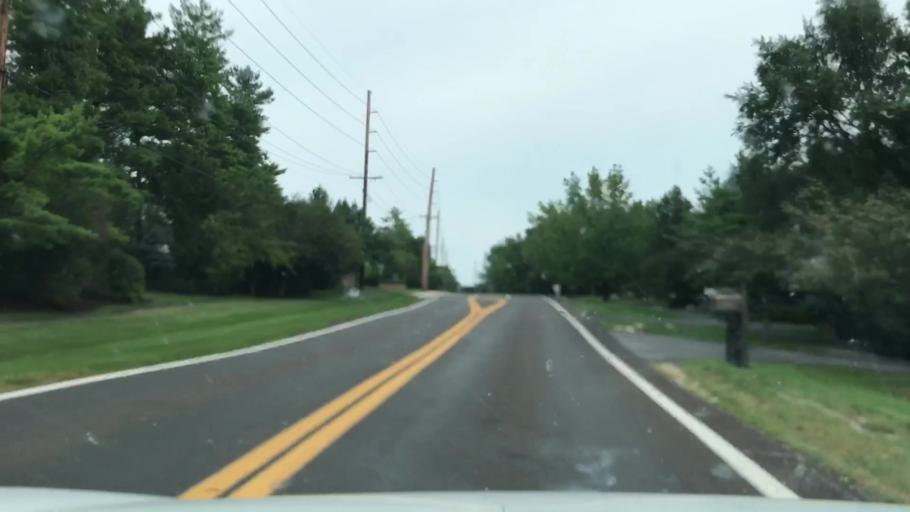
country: US
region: Missouri
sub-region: Saint Louis County
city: Clarkson Valley
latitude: 38.6330
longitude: -90.6022
